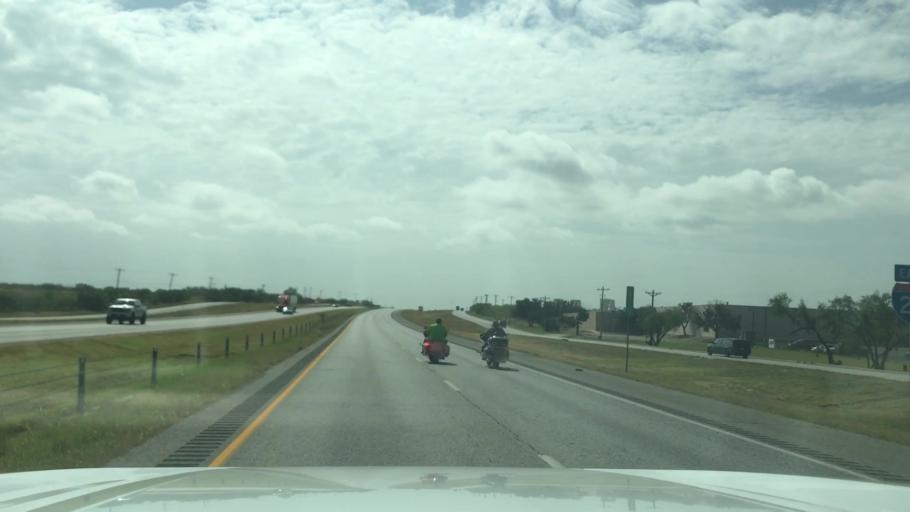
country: US
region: Texas
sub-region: Taylor County
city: Abilene
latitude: 32.4715
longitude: -99.6904
